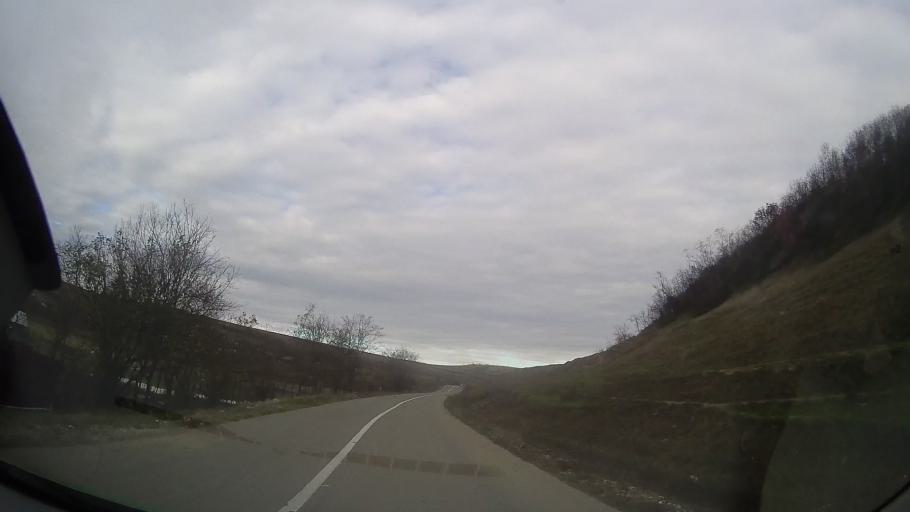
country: RO
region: Bistrita-Nasaud
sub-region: Comuna Silvasu de Campie
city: Silvasu de Campie
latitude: 46.7858
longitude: 24.2864
